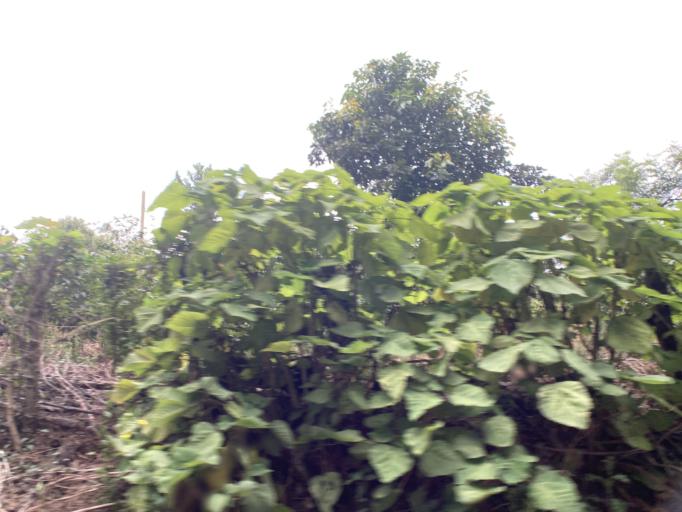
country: GT
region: Guatemala
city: Villa Canales
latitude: 14.4267
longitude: -90.5206
